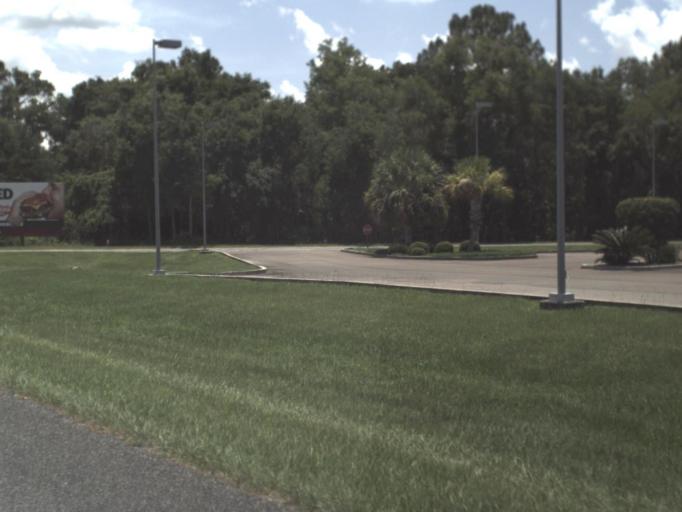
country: US
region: Florida
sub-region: Levy County
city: Chiefland
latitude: 29.5089
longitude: -82.8747
